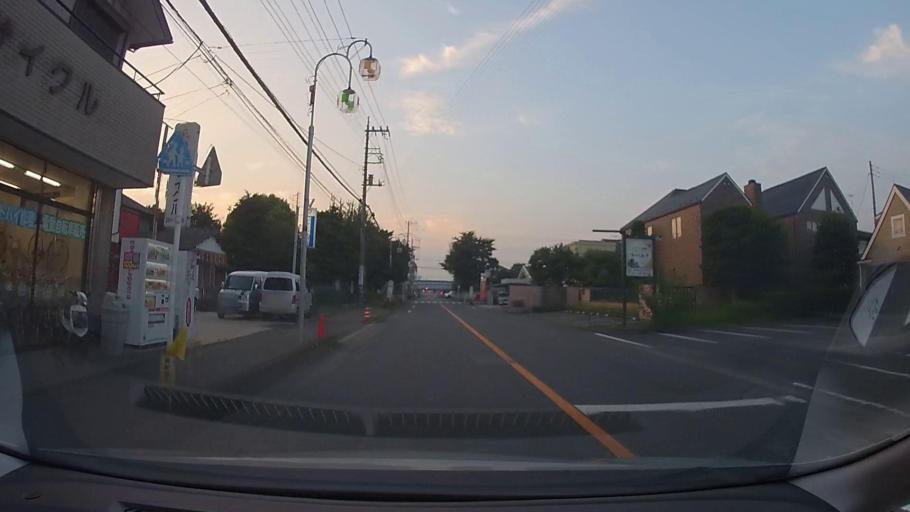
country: JP
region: Kanagawa
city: Minami-rinkan
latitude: 35.4766
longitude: 139.4543
